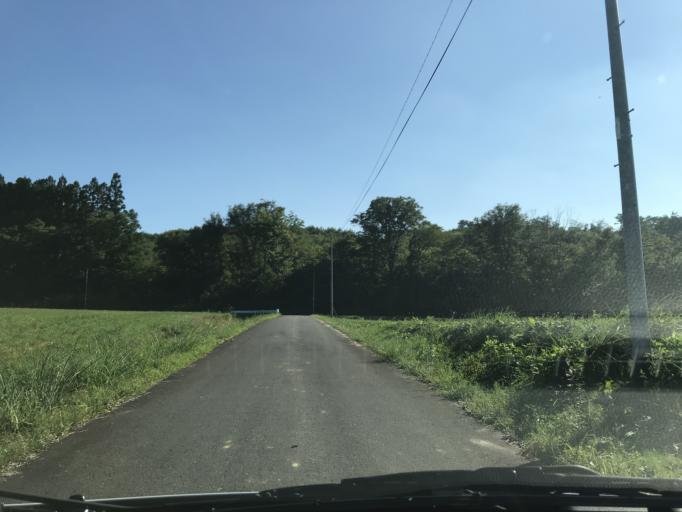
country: JP
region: Iwate
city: Mizusawa
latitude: 39.0735
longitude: 141.0389
